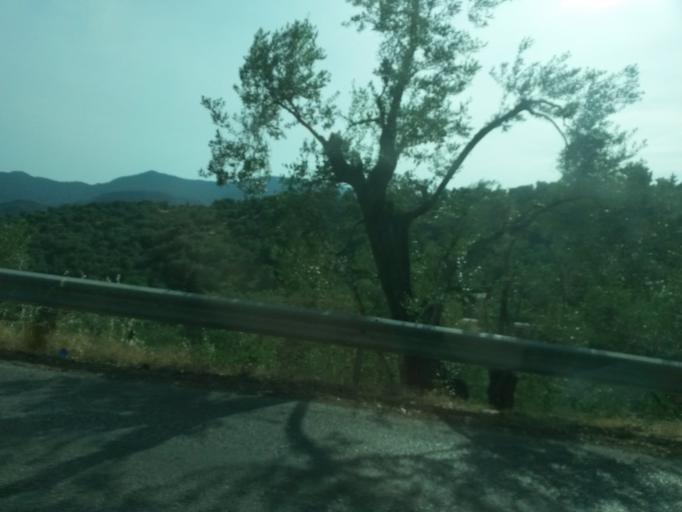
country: GR
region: North Aegean
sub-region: Nomos Lesvou
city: Palaiokipos
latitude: 39.0681
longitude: 26.4567
